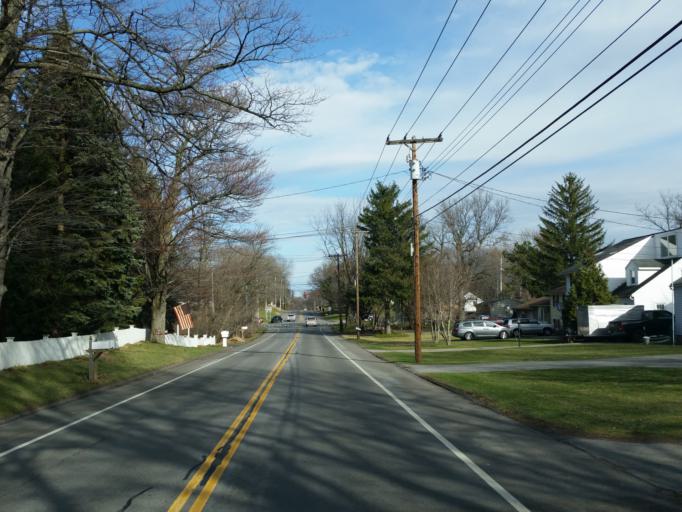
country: US
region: New York
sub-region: Monroe County
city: North Gates
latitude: 43.1162
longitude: -77.7476
